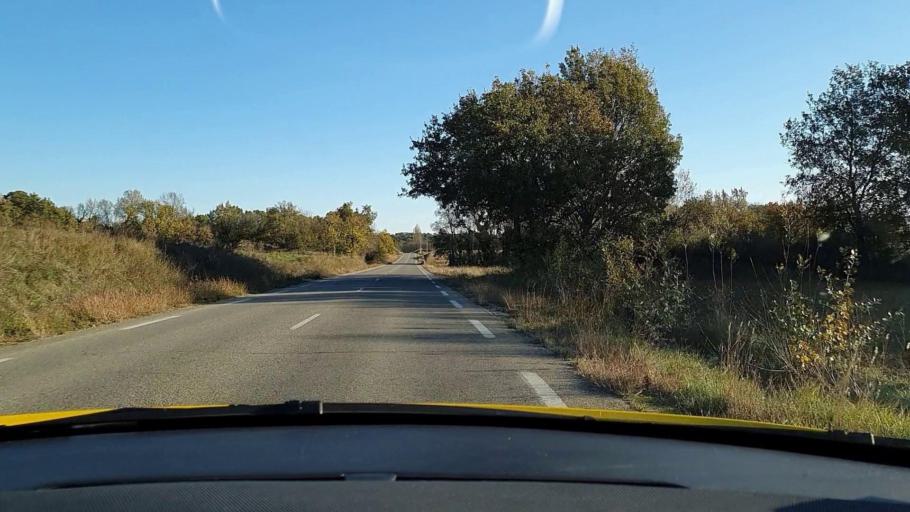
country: FR
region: Languedoc-Roussillon
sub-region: Departement du Gard
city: Salindres
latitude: 44.1801
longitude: 4.1798
